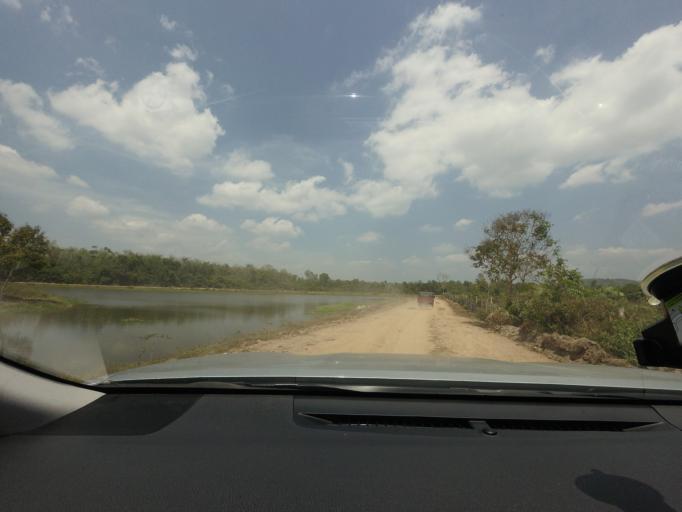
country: TH
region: Narathiwat
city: Rueso
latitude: 6.3871
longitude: 101.4988
